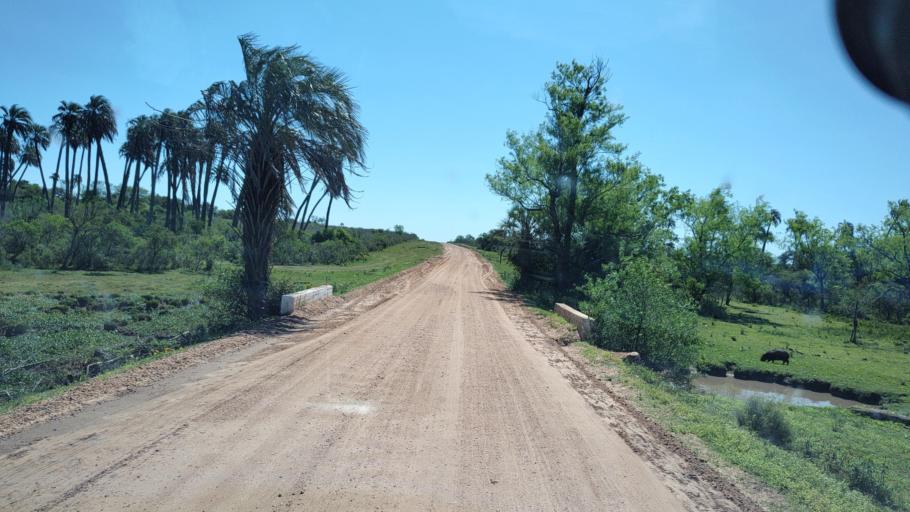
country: AR
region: Entre Rios
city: Ubajay
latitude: -31.8689
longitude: -58.2454
